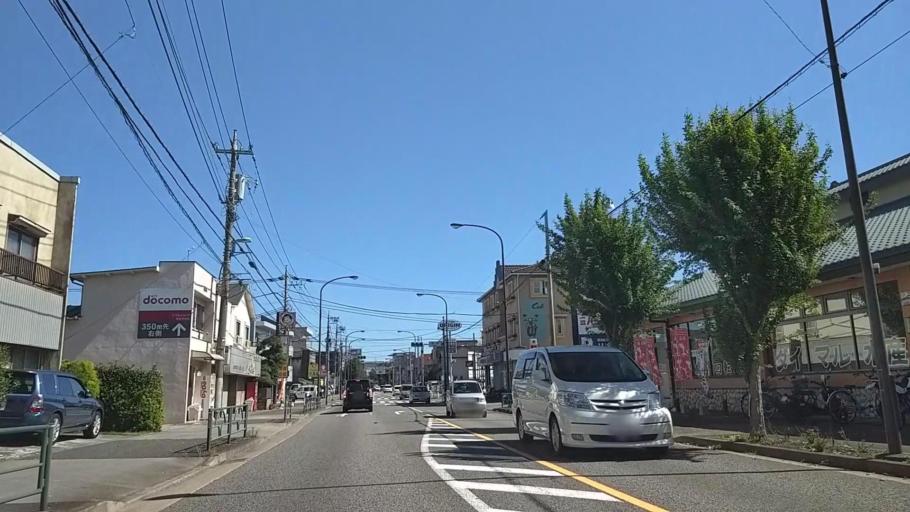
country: JP
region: Tokyo
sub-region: Machida-shi
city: Machida
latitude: 35.5777
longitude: 139.4131
